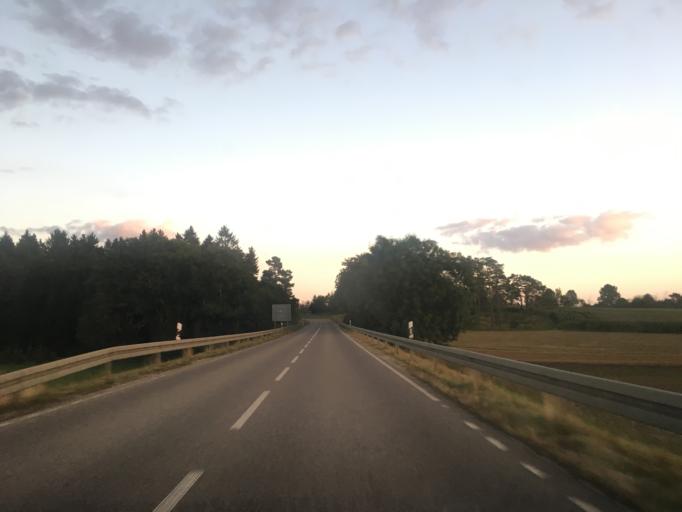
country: DE
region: Baden-Wuerttemberg
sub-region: Tuebingen Region
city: Hayingen
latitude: 48.2967
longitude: 9.4576
